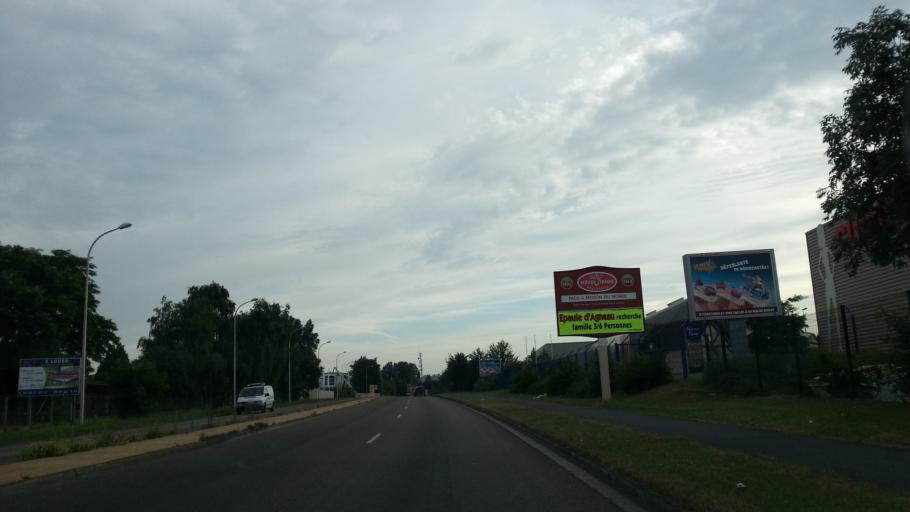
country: FR
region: Picardie
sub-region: Departement de l'Oise
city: Saint-Maximin
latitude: 49.2403
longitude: 2.4658
